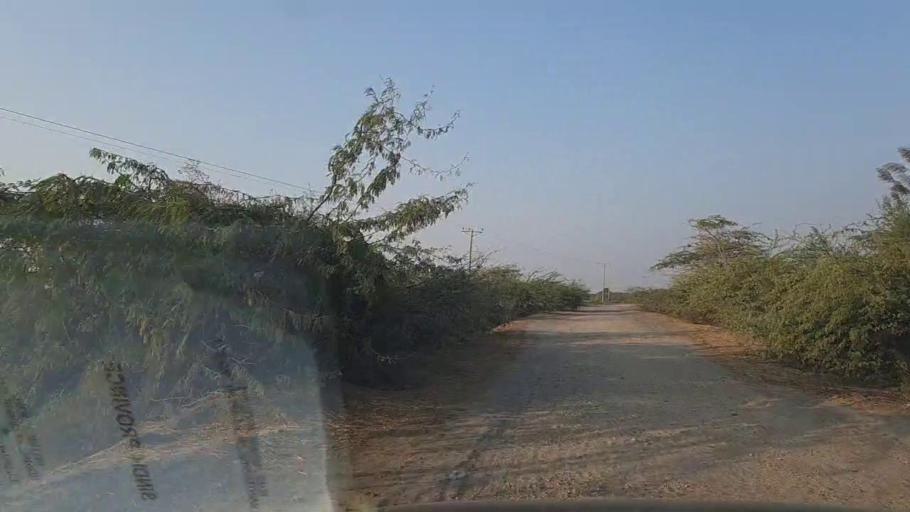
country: PK
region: Sindh
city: Keti Bandar
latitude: 24.2813
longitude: 67.5875
